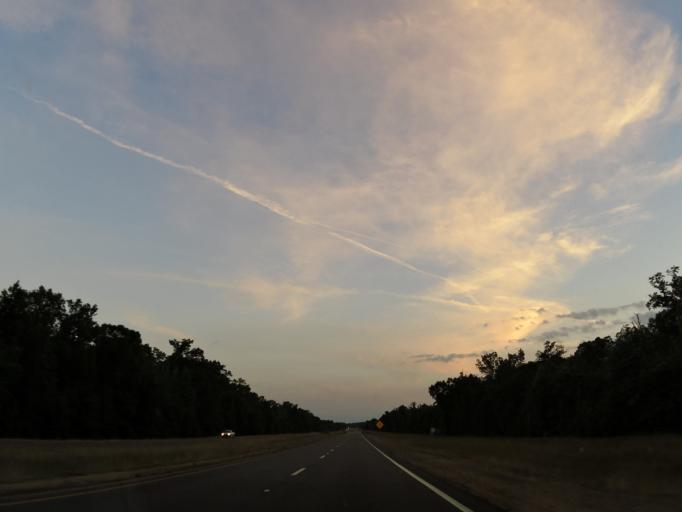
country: US
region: Mississippi
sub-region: Kemper County
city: De Kalb
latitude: 32.7070
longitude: -88.4827
